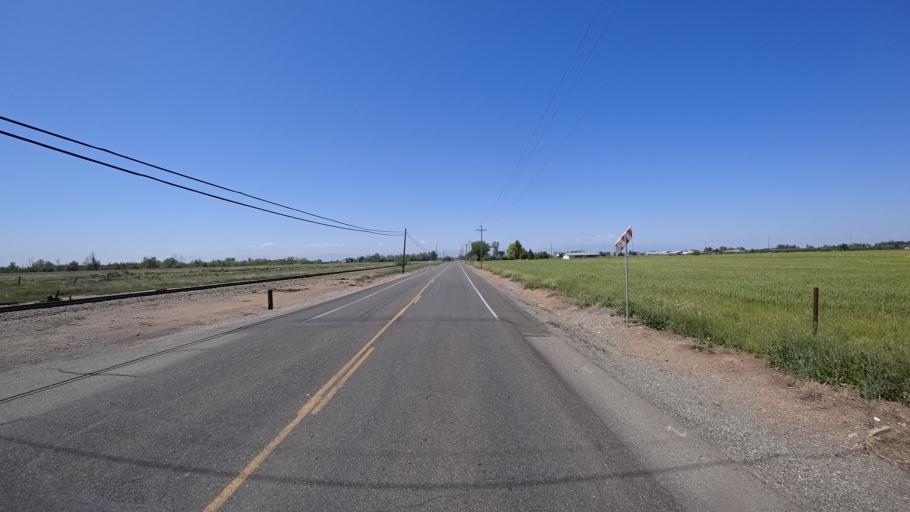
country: US
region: California
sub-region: Glenn County
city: Orland
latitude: 39.7686
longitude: -122.1411
